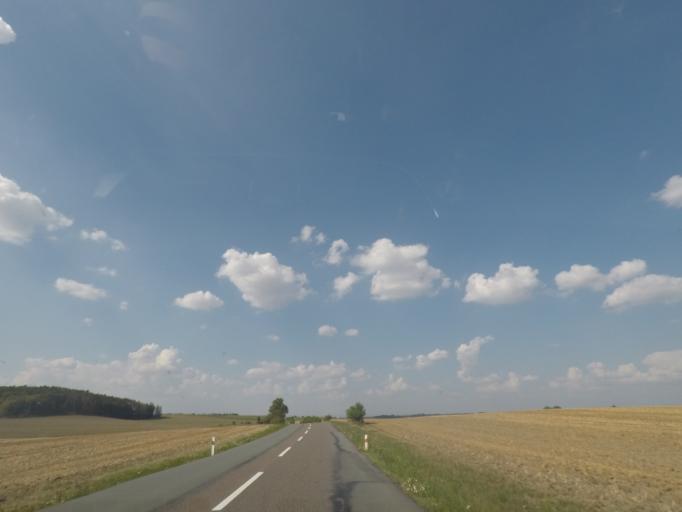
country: CZ
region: Kralovehradecky
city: Dolni Cernilov
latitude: 50.2500
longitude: 15.9652
